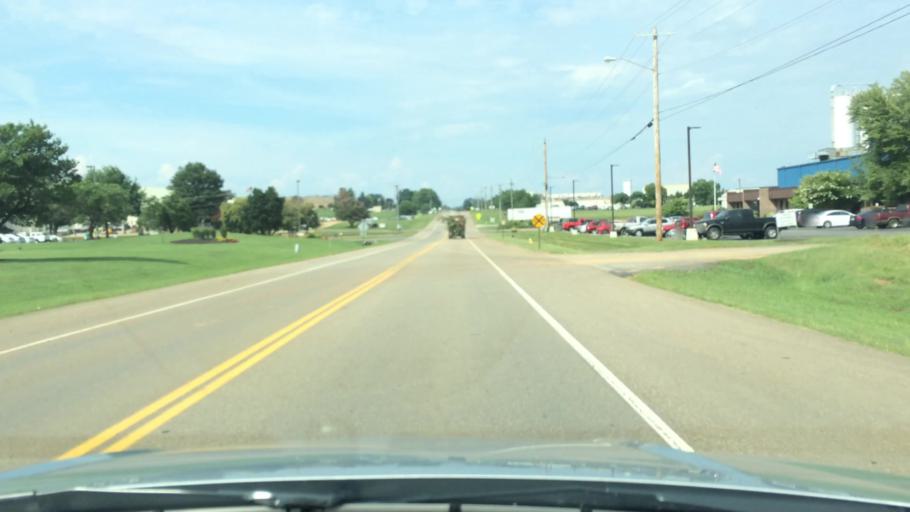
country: US
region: Tennessee
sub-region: Jefferson County
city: Jefferson City
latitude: 36.1644
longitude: -83.3952
